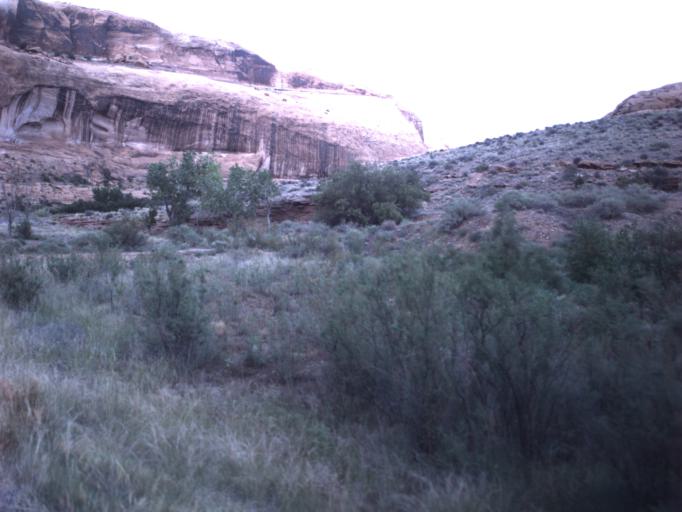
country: US
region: Utah
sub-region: Grand County
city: Moab
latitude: 38.6115
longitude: -109.5573
